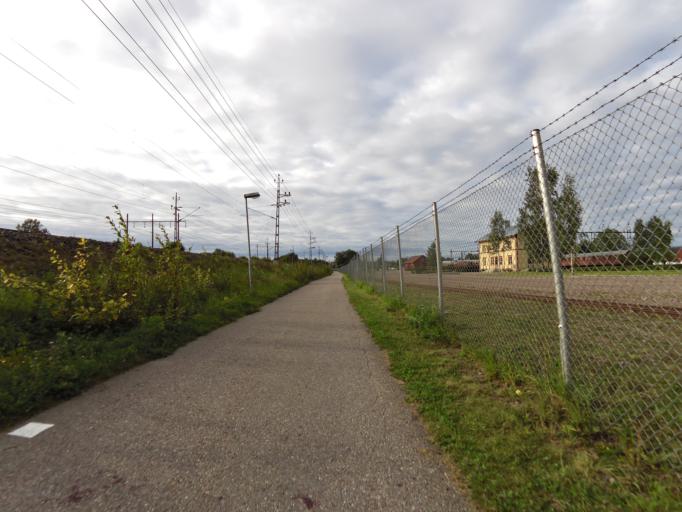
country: SE
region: Gaevleborg
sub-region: Gavle Kommun
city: Gavle
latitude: 60.6623
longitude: 17.1697
